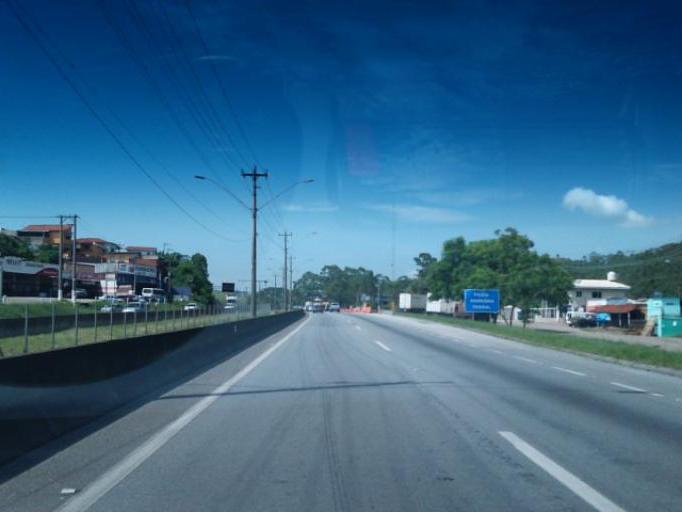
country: BR
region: Sao Paulo
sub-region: Itapecerica Da Serra
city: Itapecerica da Serra
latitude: -23.6888
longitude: -46.8619
